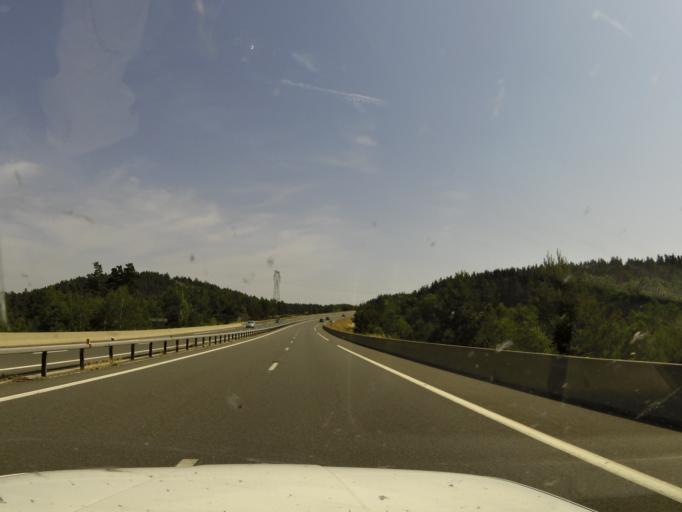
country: FR
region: Languedoc-Roussillon
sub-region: Departement de la Lozere
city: Aumont-Aubrac
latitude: 44.7923
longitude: 3.2934
